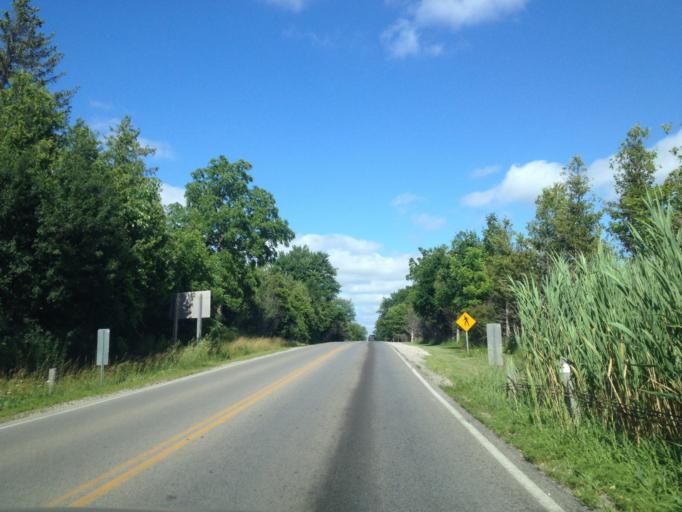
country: CA
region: Ontario
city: London
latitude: 43.0317
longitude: -81.3113
